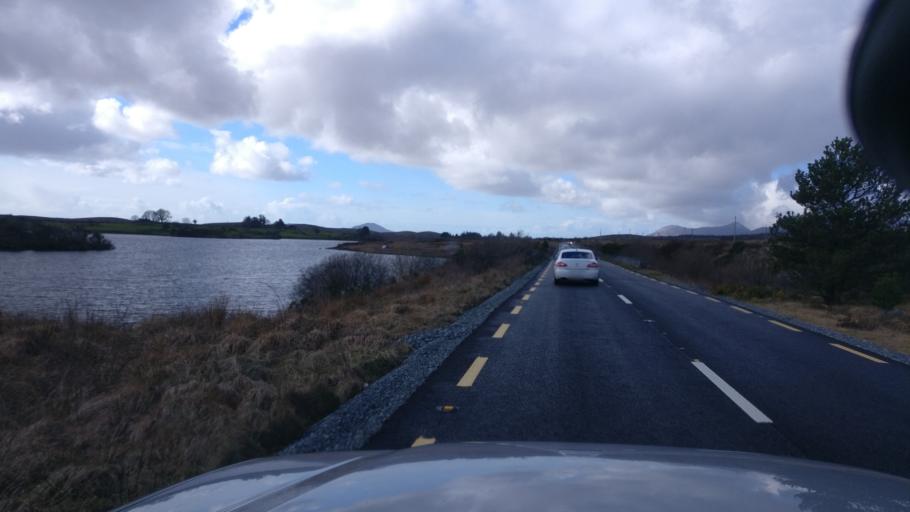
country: IE
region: Connaught
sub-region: County Galway
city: Oughterard
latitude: 53.4554
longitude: -9.6138
